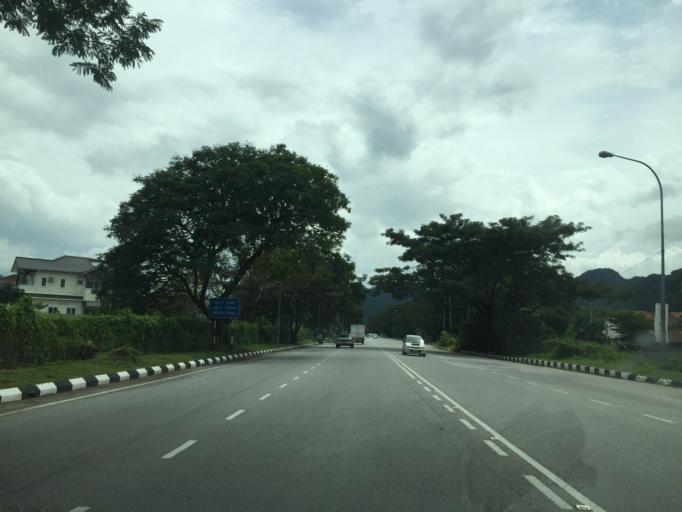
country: MY
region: Perak
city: Ipoh
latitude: 4.5688
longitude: 101.1161
